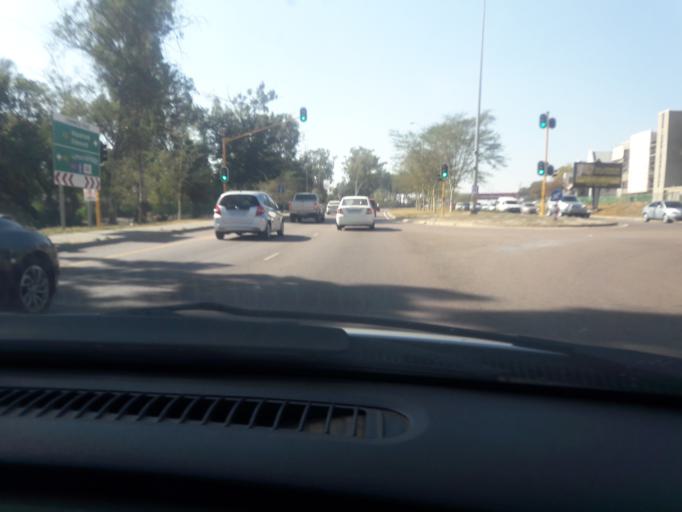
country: ZA
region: Gauteng
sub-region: City of Tshwane Metropolitan Municipality
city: Pretoria
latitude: -25.7656
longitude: 28.3110
